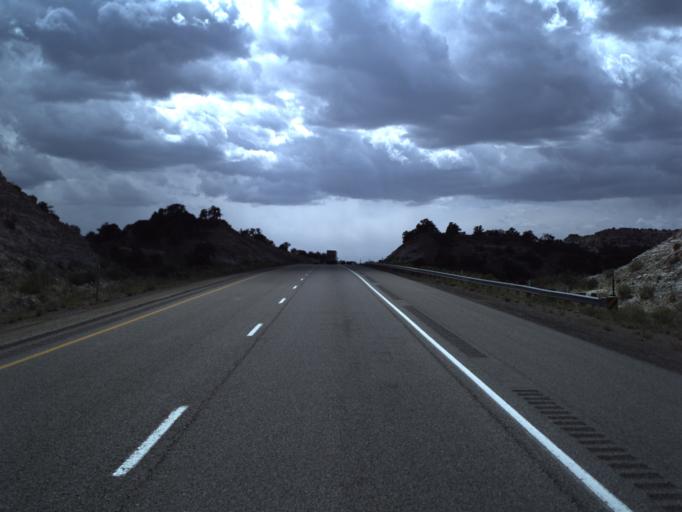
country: US
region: Utah
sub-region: Emery County
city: Ferron
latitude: 38.8506
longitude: -110.8845
